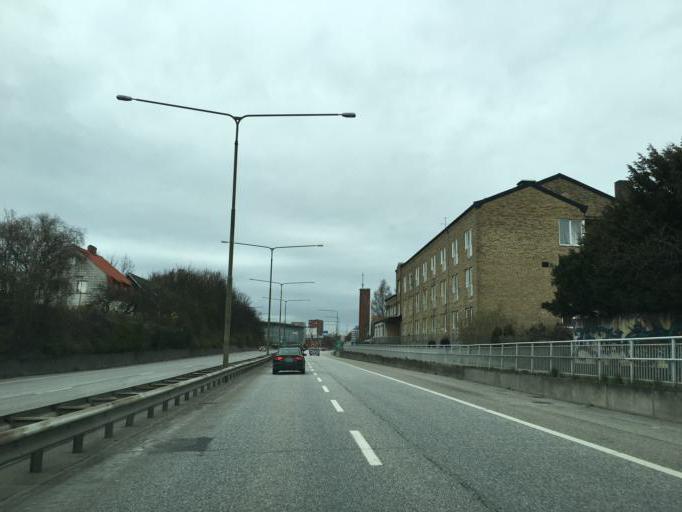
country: SE
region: Skane
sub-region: Malmo
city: Malmoe
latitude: 55.5759
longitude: 13.0051
